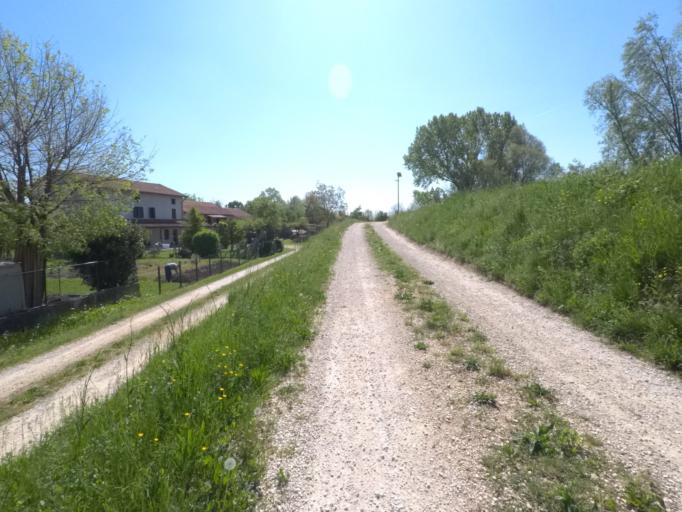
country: IT
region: Veneto
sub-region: Provincia di Treviso
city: Portobuffole
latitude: 45.8773
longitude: 12.5350
